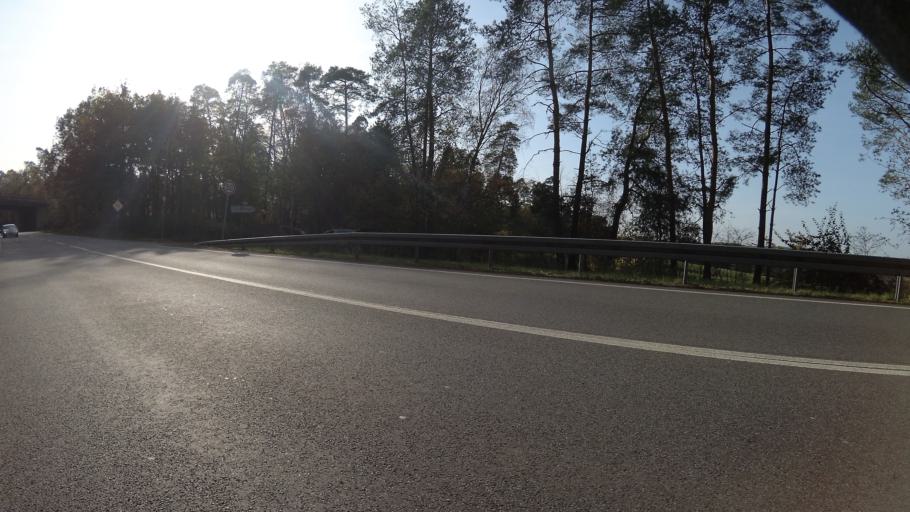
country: DE
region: Saarland
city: Bexbach
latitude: 49.3388
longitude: 7.2926
